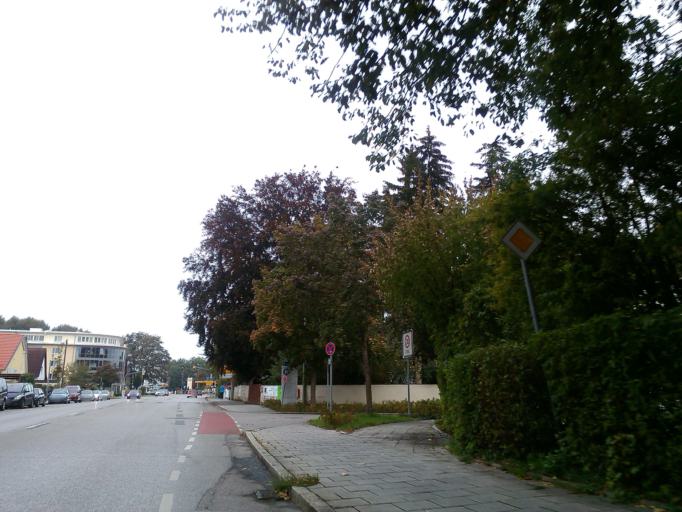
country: DE
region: Bavaria
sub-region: Upper Bavaria
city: Grobenzell
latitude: 48.1906
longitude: 11.3759
